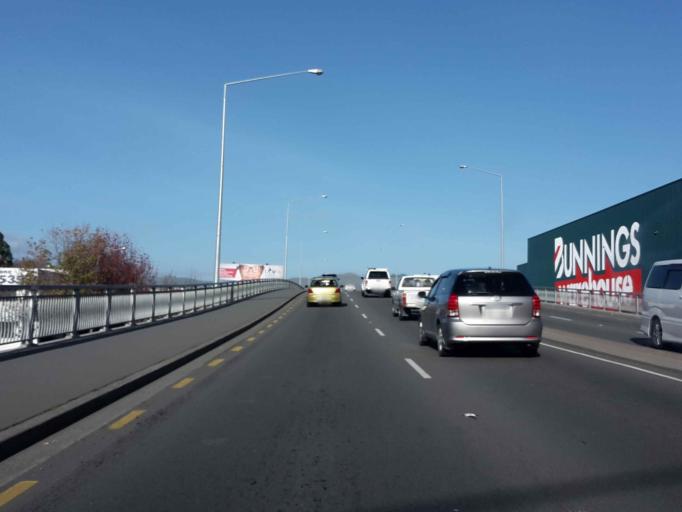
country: NZ
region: Canterbury
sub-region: Christchurch City
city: Christchurch
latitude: -43.5376
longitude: 172.6081
